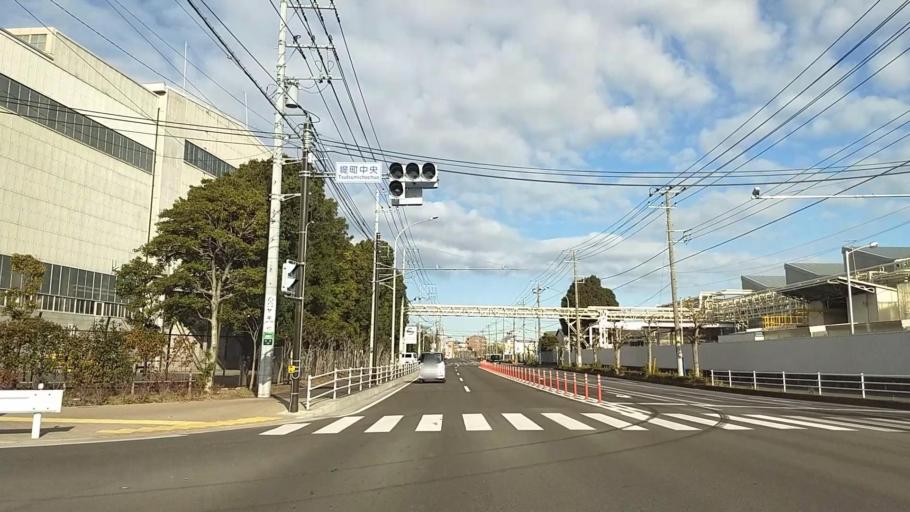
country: JP
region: Kanagawa
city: Hiratsuka
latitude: 35.3376
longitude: 139.3573
